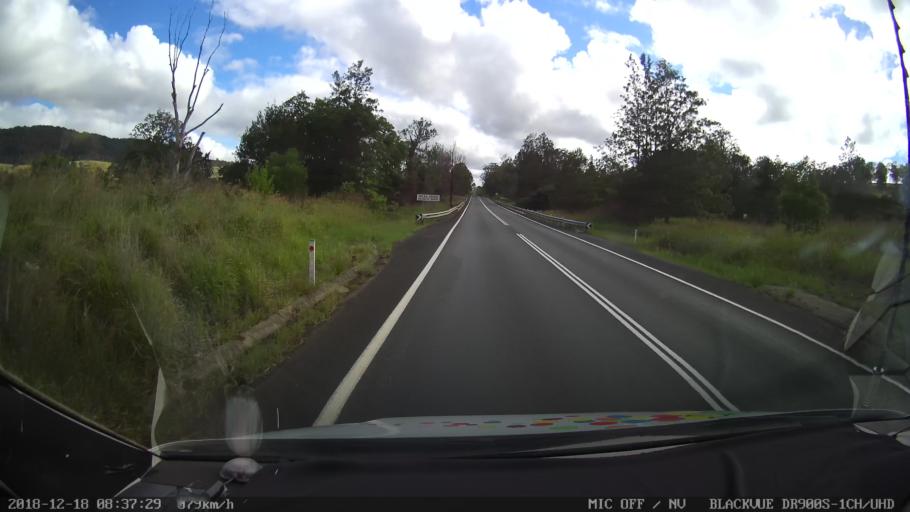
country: AU
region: New South Wales
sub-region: Kyogle
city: Kyogle
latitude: -28.2638
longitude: 152.8180
